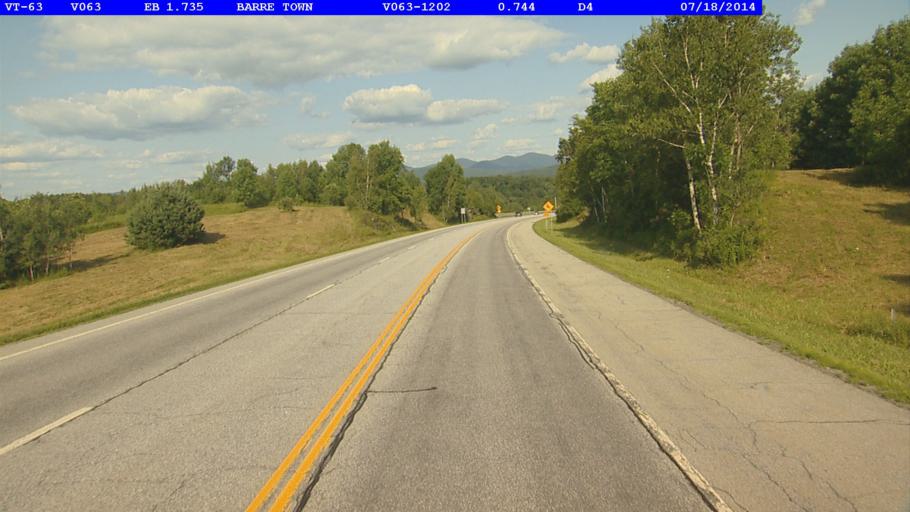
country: US
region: Vermont
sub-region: Washington County
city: South Barre
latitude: 44.1654
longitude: -72.5443
